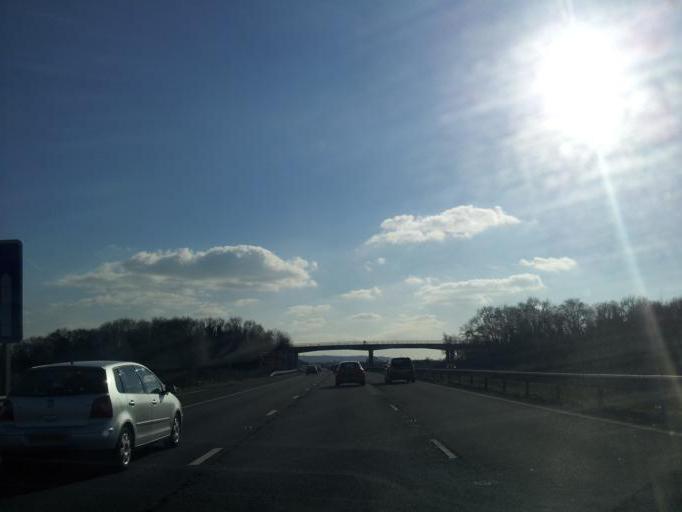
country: GB
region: England
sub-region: North Somerset
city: St. Georges
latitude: 51.3761
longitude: -2.8835
